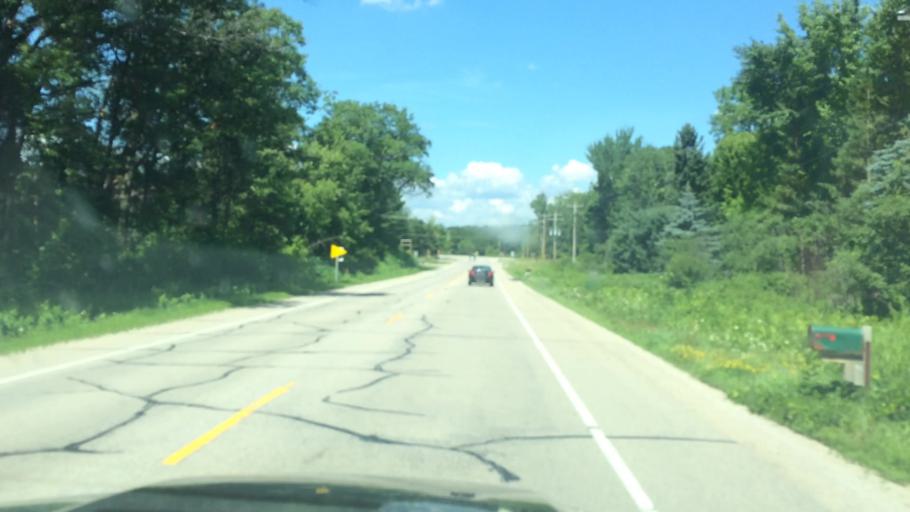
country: US
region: Wisconsin
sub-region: Marinette County
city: Peshtigo
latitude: 45.1035
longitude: -87.7481
